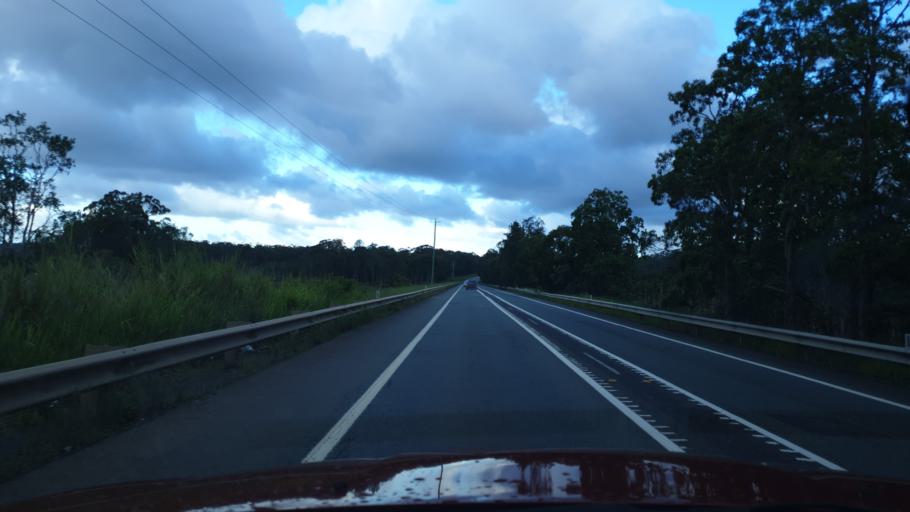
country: AU
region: Queensland
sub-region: Sunshine Coast
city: Little Mountain
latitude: -26.7987
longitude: 152.9876
